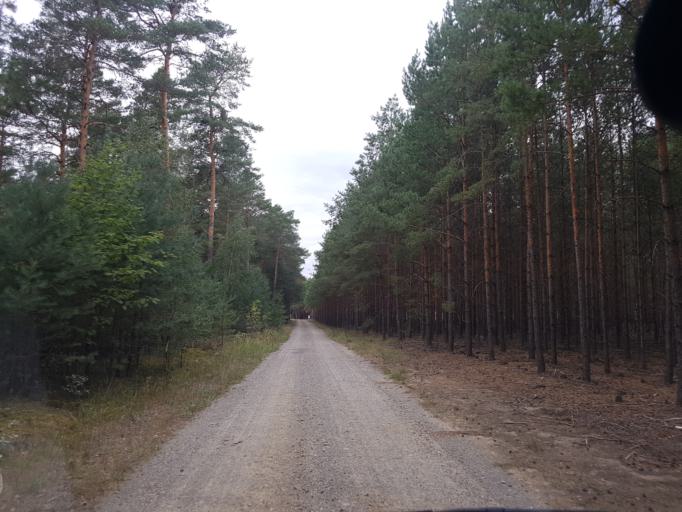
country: DE
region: Brandenburg
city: Sallgast
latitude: 51.6423
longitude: 13.8426
